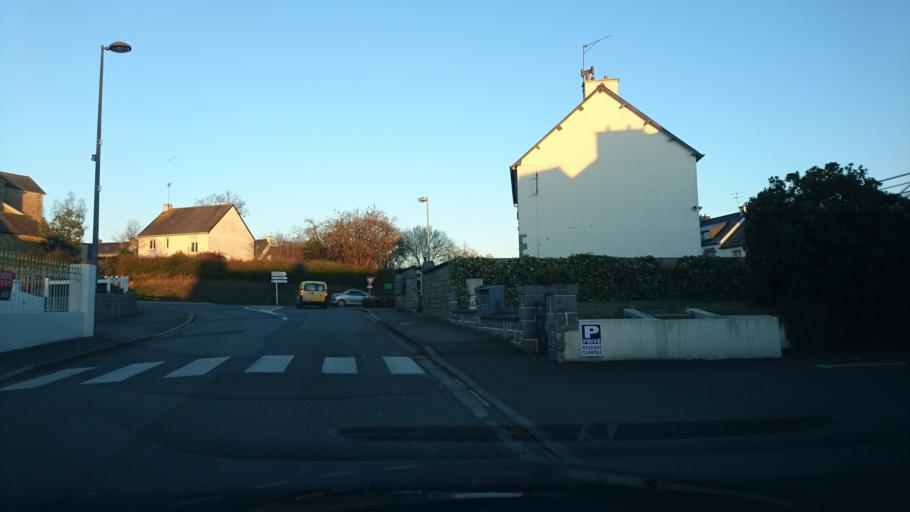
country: FR
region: Brittany
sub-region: Departement des Cotes-d'Armor
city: Pledran
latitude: 48.4451
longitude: -2.7437
